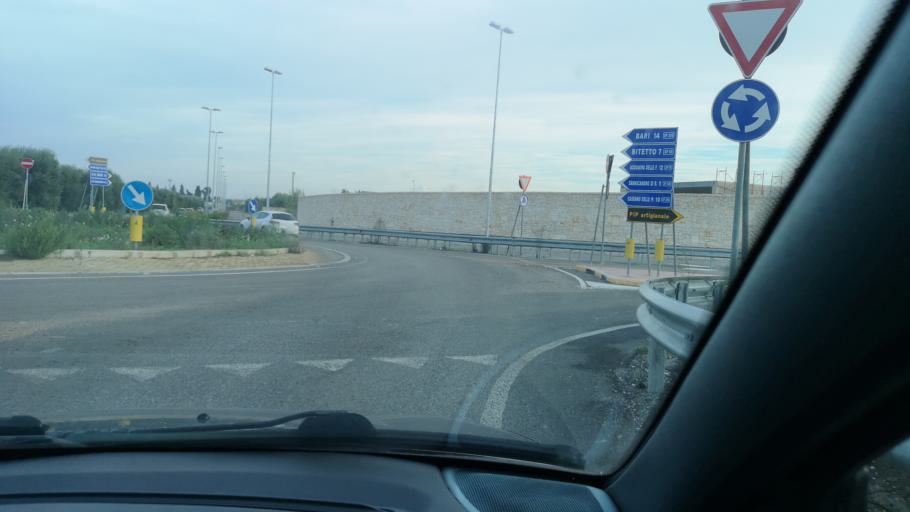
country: IT
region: Apulia
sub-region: Provincia di Bari
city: Sannicandro di Bari
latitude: 40.9856
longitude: 16.7961
